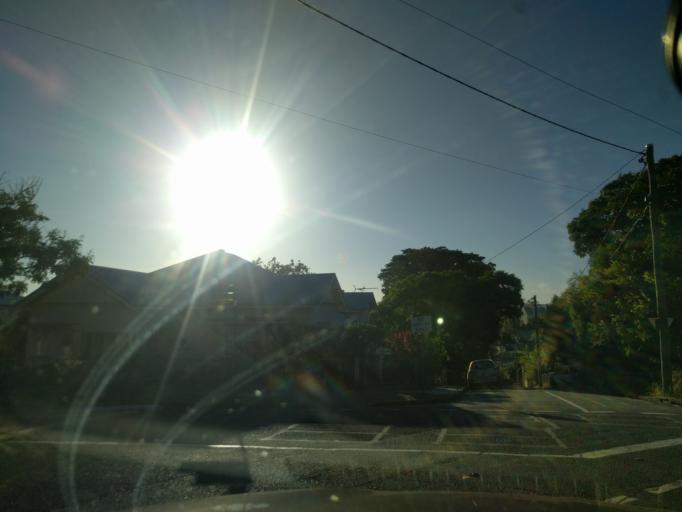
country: AU
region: Queensland
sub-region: Brisbane
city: Annerley
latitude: -27.5013
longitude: 153.0296
